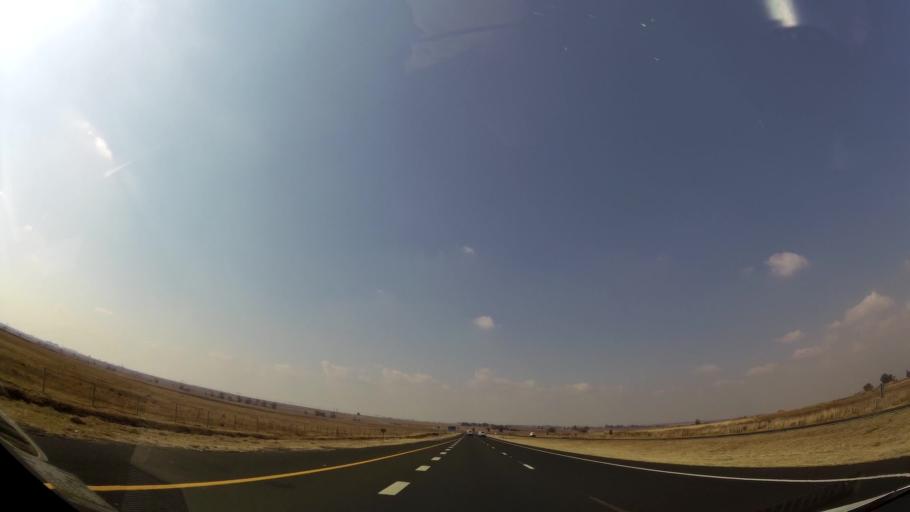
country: ZA
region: Gauteng
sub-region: Ekurhuleni Metropolitan Municipality
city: Springs
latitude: -26.1634
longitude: 28.4503
